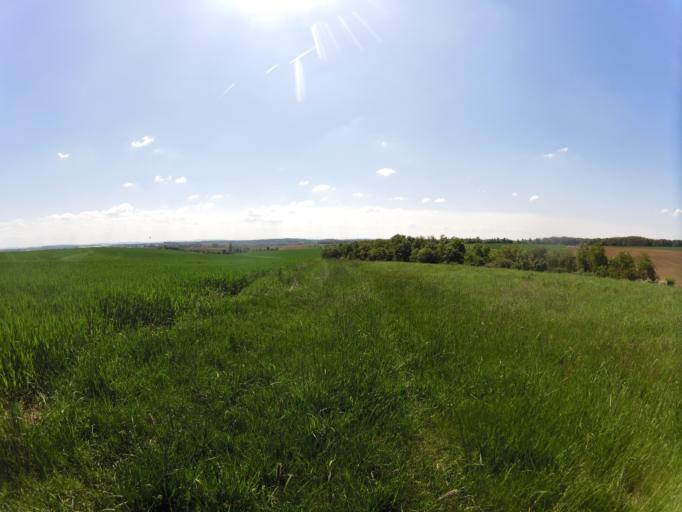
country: DE
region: Bavaria
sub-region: Regierungsbezirk Unterfranken
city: Kurnach
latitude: 49.8782
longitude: 10.0007
